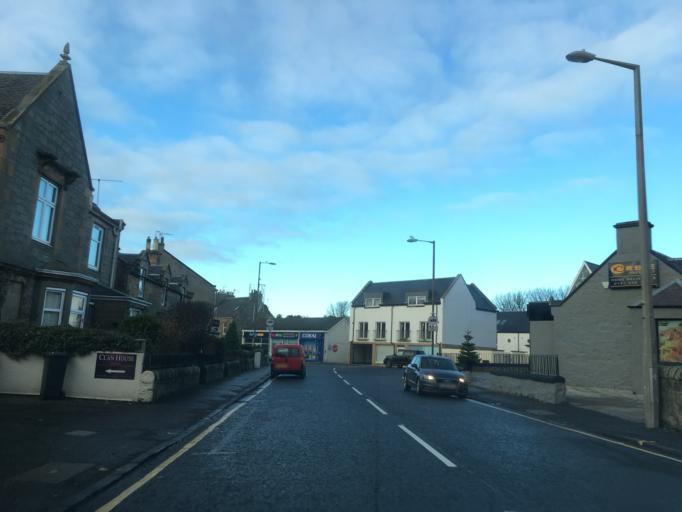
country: GB
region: Scotland
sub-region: Edinburgh
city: Colinton
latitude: 55.9651
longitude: -3.2694
